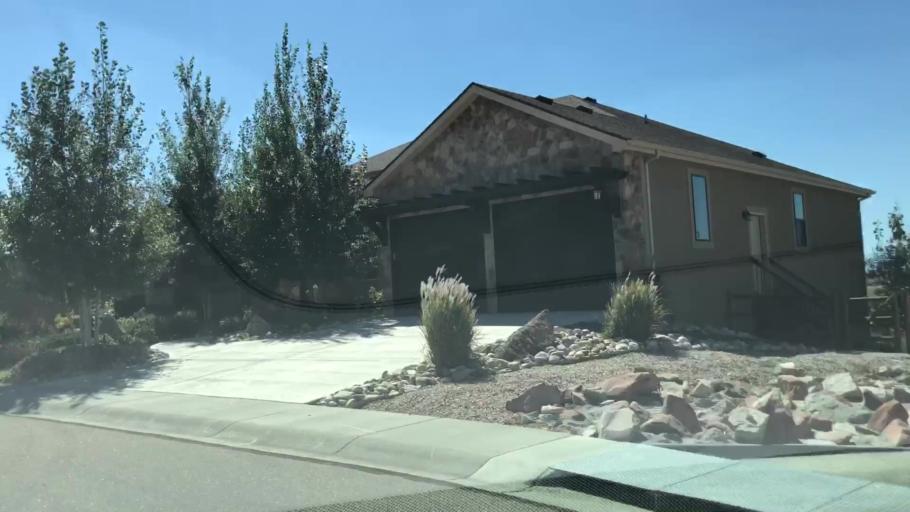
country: US
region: Colorado
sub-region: Weld County
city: Windsor
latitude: 40.4556
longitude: -104.9590
